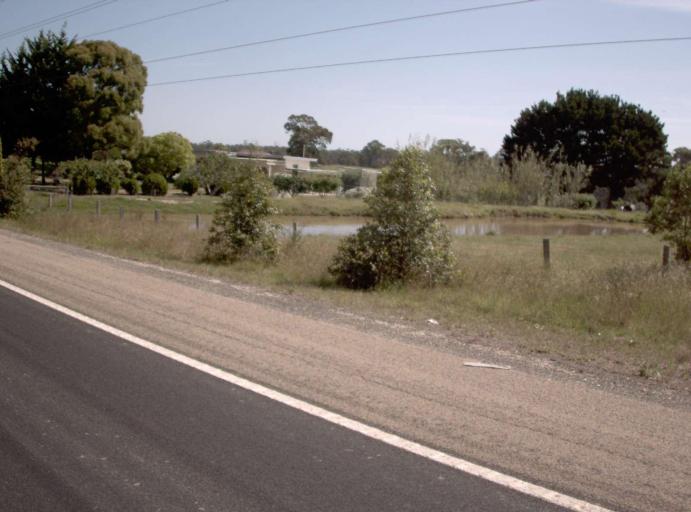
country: AU
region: Victoria
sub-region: East Gippsland
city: Lakes Entrance
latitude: -37.8448
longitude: 147.9292
